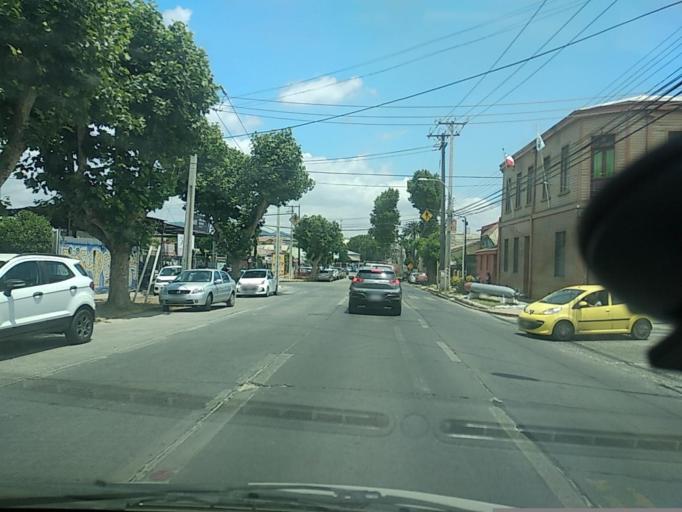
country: CL
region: Valparaiso
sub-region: Provincia de Marga Marga
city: Quilpue
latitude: -33.0443
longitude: -71.4366
